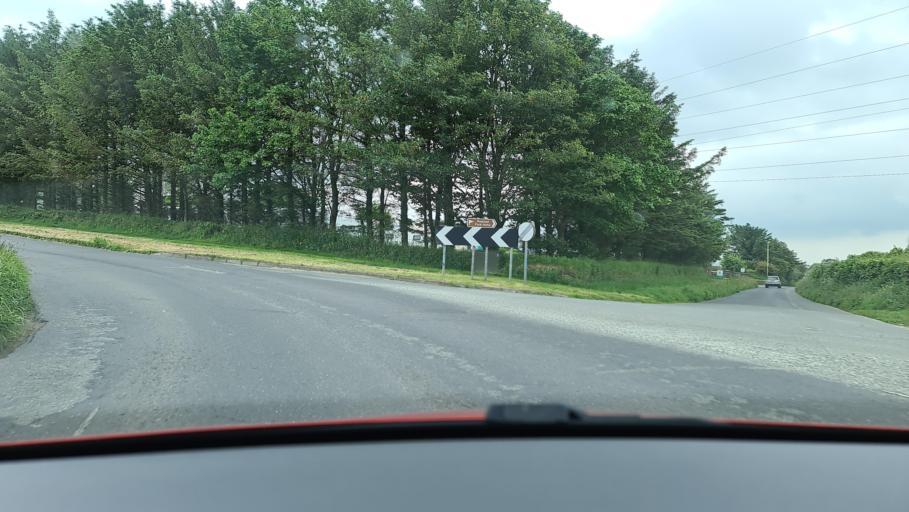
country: GB
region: England
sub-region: Cornwall
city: Camelford
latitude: 50.6161
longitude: -4.6888
